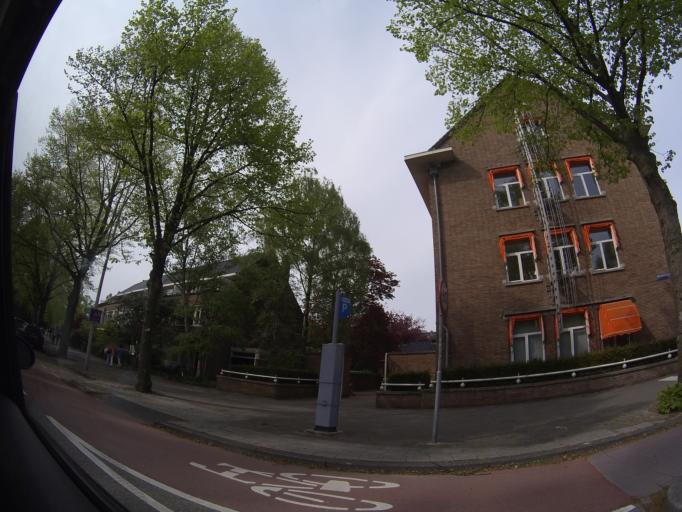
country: NL
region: North Holland
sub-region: Gemeente Amsterdam
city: Amsterdam
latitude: 52.3446
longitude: 4.8846
